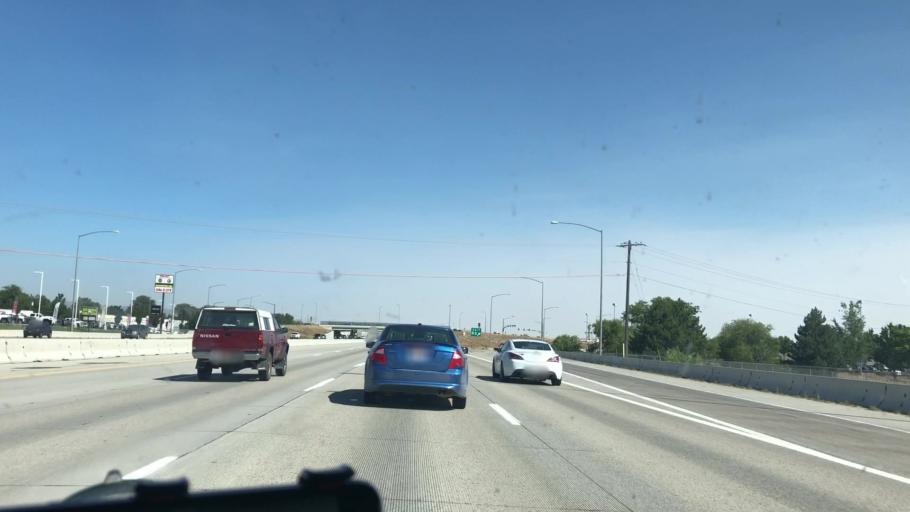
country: US
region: Idaho
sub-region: Ada County
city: Garden City
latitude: 43.5780
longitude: -116.2492
